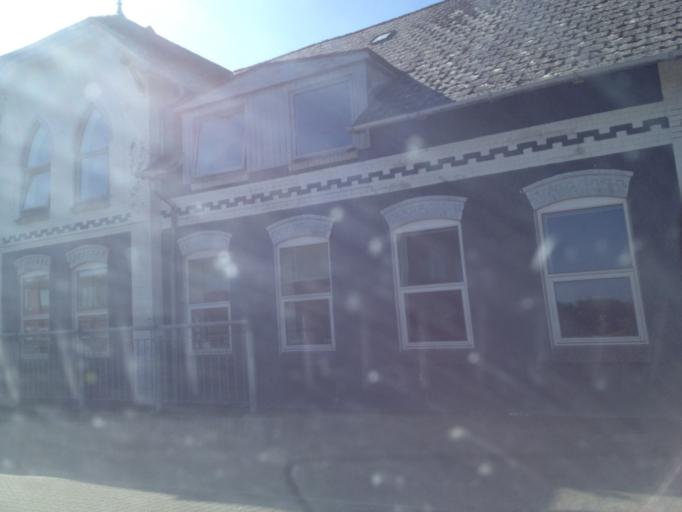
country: DK
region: South Denmark
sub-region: Haderslev Kommune
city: Vojens
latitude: 55.3141
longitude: 9.2883
